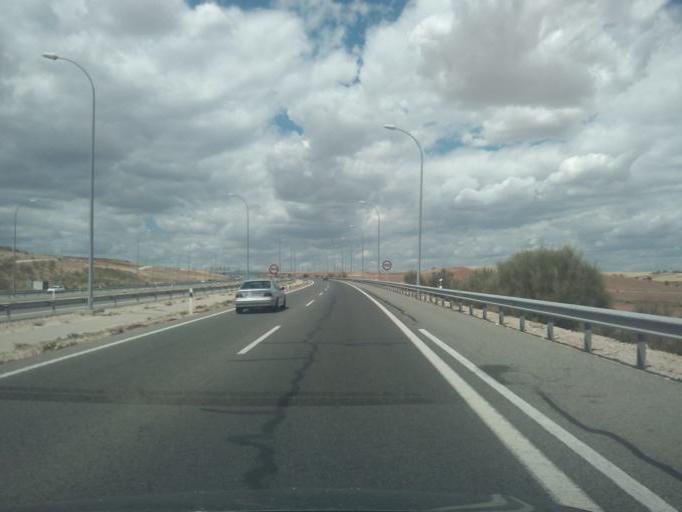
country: ES
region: Madrid
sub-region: Provincia de Madrid
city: Ajalvir
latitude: 40.5180
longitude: -3.5026
